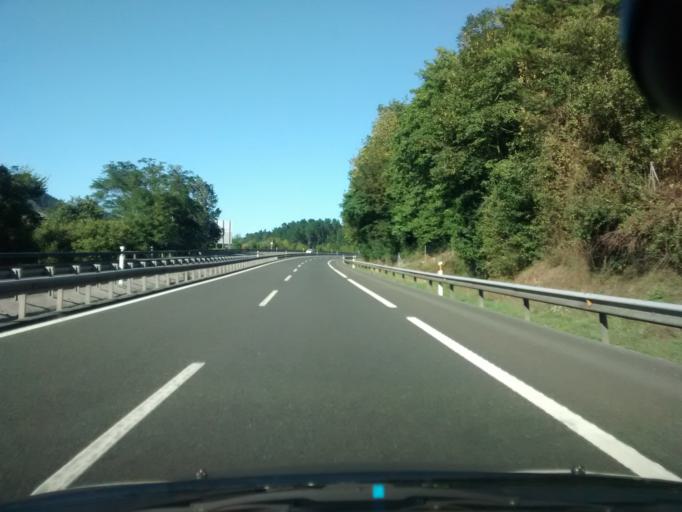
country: ES
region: Basque Country
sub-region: Provincia de Guipuzcoa
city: Elgoibar
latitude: 43.2056
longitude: -2.4213
